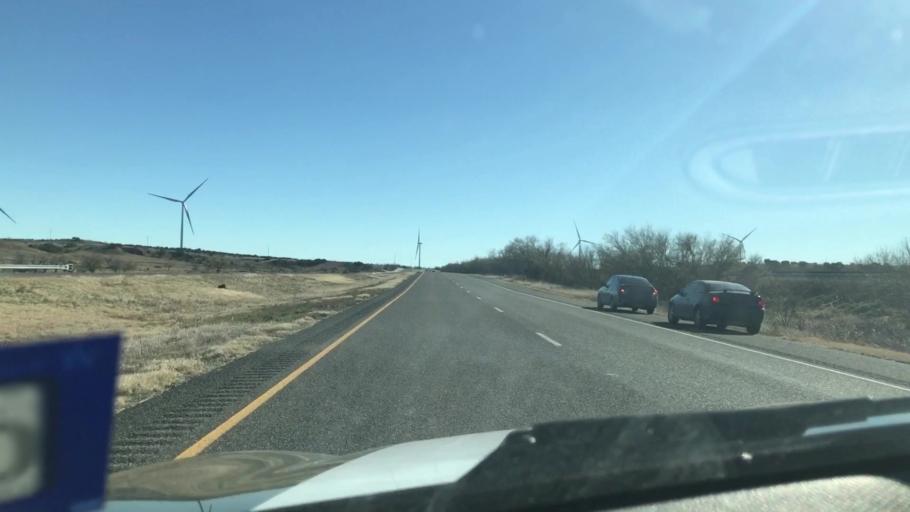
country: US
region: Texas
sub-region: Scurry County
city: Snyder
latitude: 32.8987
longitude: -101.0558
